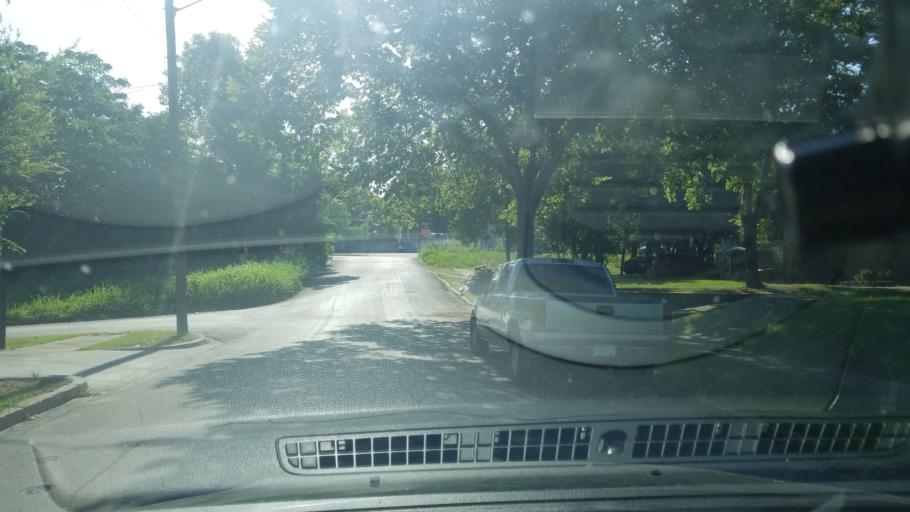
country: US
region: Texas
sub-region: Dallas County
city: Dallas
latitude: 32.7259
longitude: -96.8238
